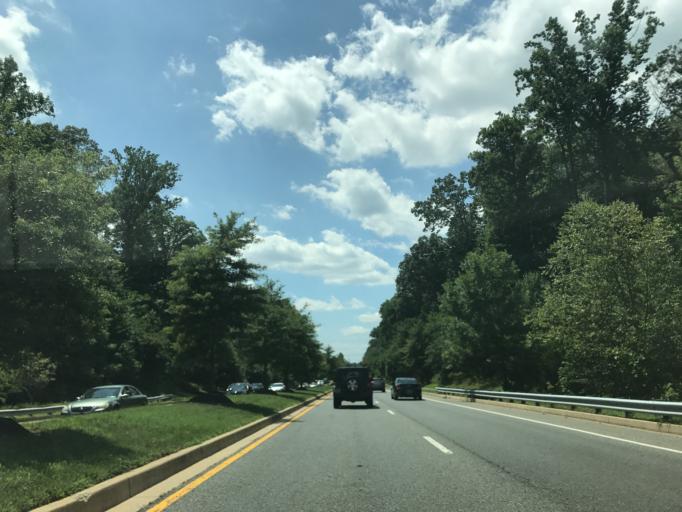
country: US
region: Maryland
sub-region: Prince George's County
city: Bowie
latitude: 38.9732
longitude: -76.7619
